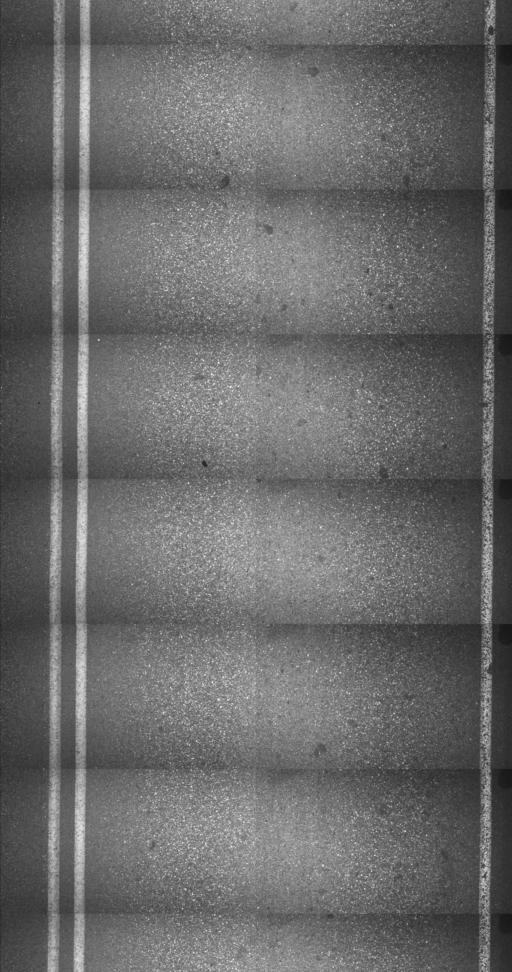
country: US
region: Vermont
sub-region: Lamoille County
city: Hyde Park
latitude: 44.7040
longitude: -72.5573
